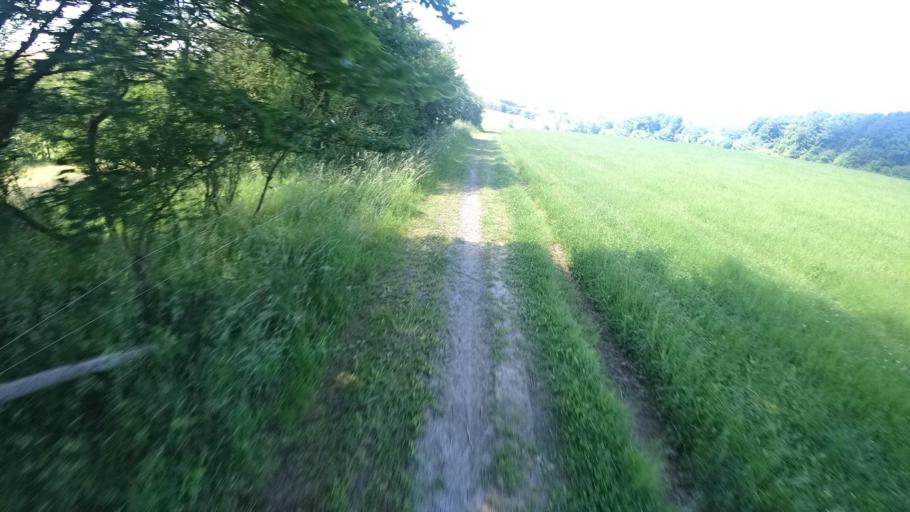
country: DE
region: Rheinland-Pfalz
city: Giesenhausen
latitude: 50.7022
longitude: 7.7053
